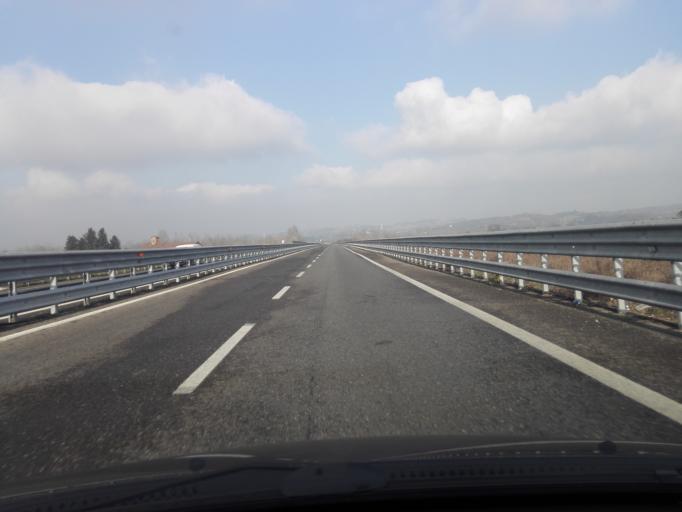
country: IT
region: Piedmont
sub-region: Provincia di Alessandria
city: Valle San Bartolomeo
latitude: 44.9238
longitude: 8.6378
